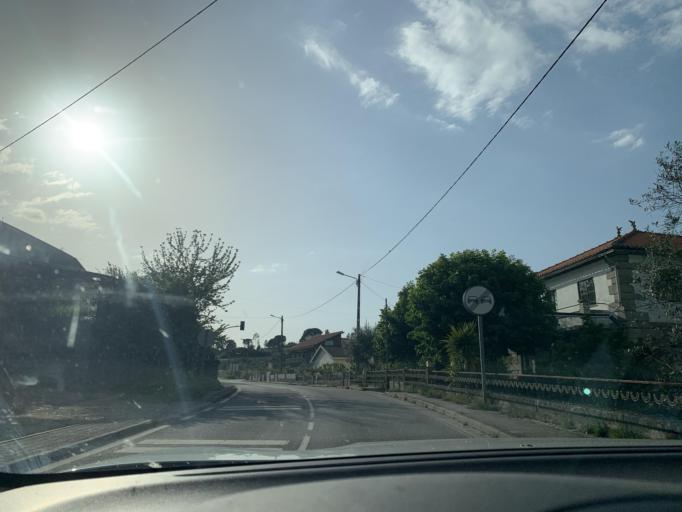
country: PT
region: Viseu
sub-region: Mangualde
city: Mangualde
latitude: 40.5639
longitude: -7.7178
